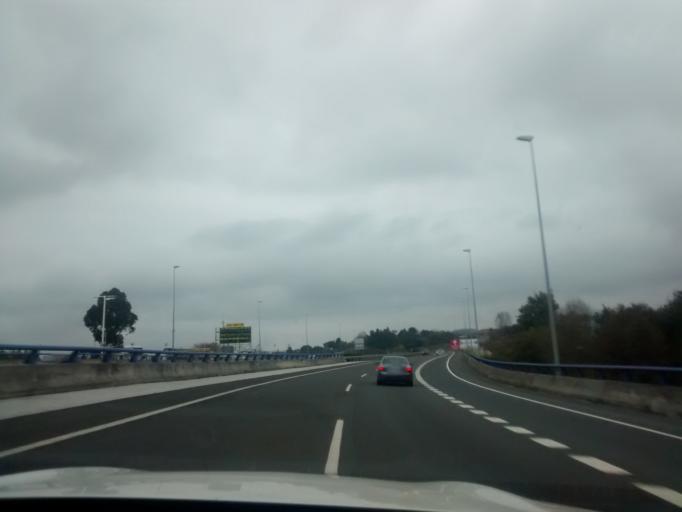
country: ES
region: Cantabria
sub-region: Provincia de Cantabria
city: Cartes
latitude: 43.3186
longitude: -4.0658
